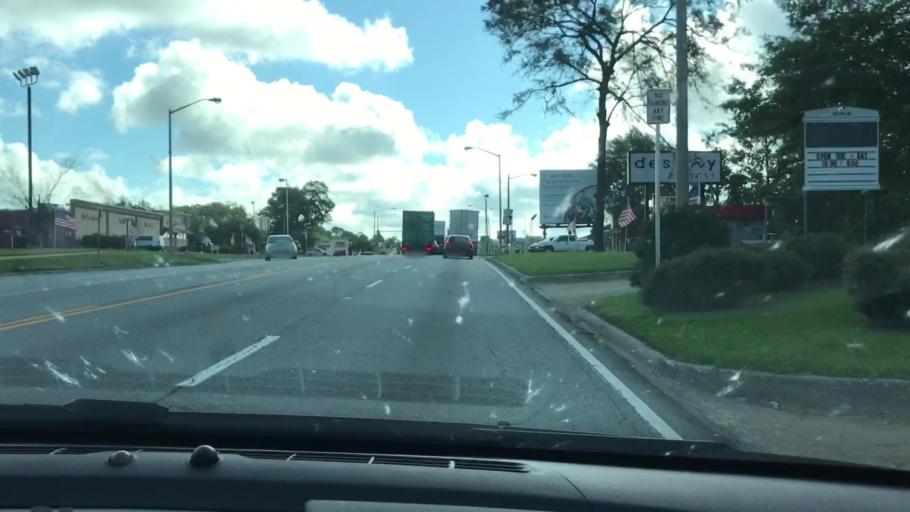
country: US
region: Georgia
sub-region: Worth County
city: Sylvester
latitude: 31.5307
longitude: -83.8395
